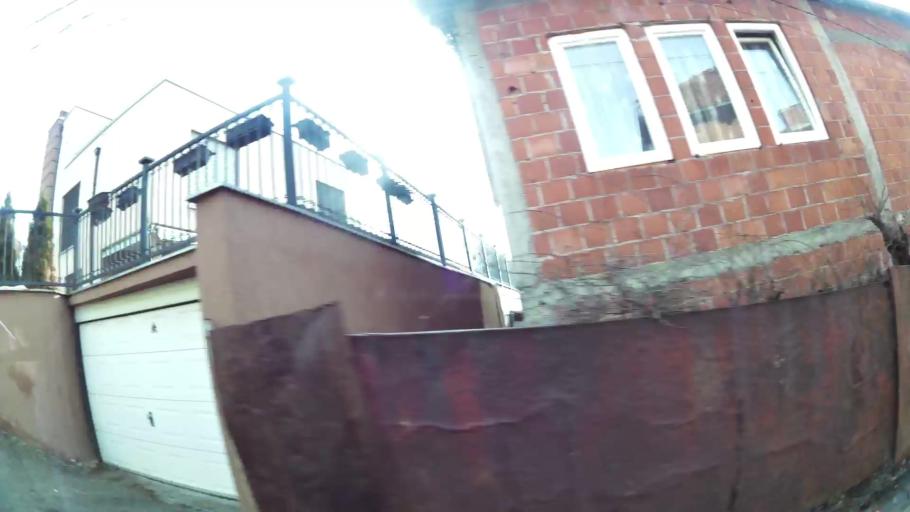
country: XK
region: Pristina
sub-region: Komuna e Prishtines
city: Pristina
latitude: 42.6711
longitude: 21.1779
